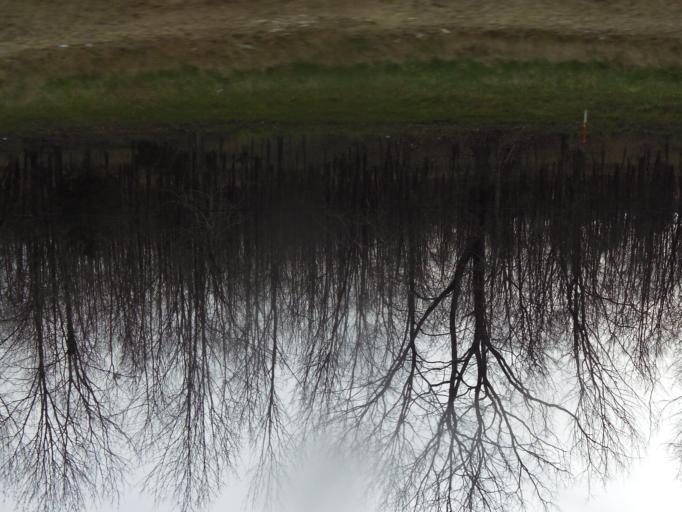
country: US
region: Alabama
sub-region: Montgomery County
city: Montgomery
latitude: 32.3152
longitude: -86.2285
